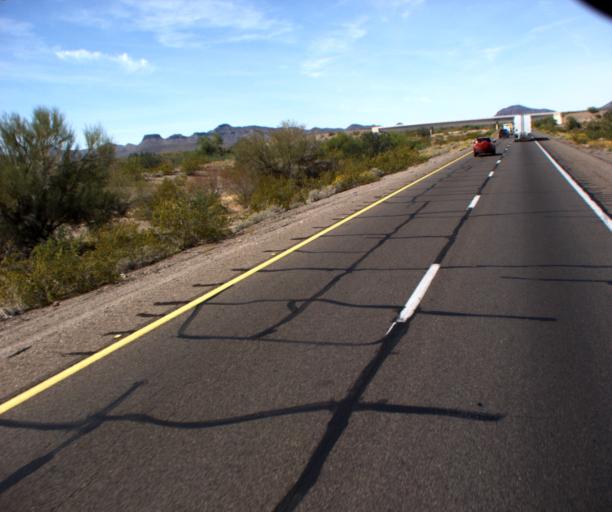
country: US
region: Arizona
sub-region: La Paz County
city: Quartzsite
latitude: 33.6561
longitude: -113.9614
